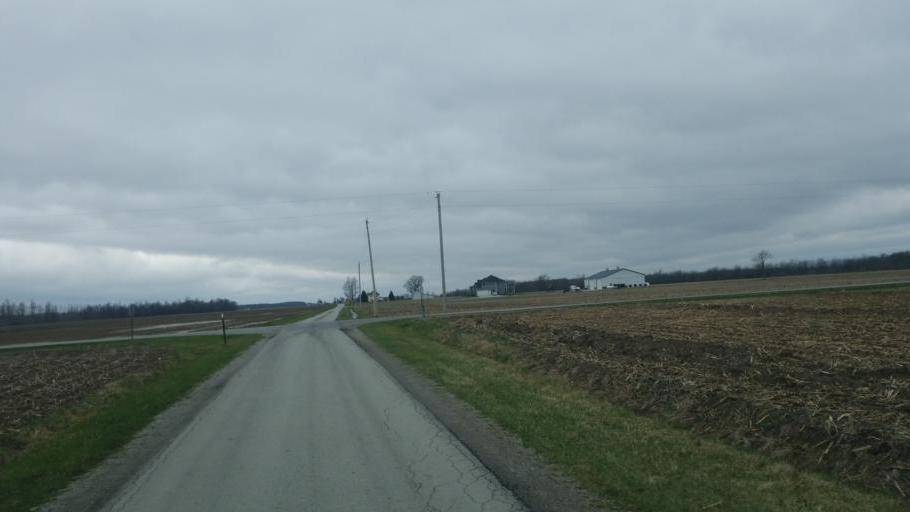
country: US
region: Ohio
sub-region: Hardin County
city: Forest
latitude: 40.7234
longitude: -83.4772
